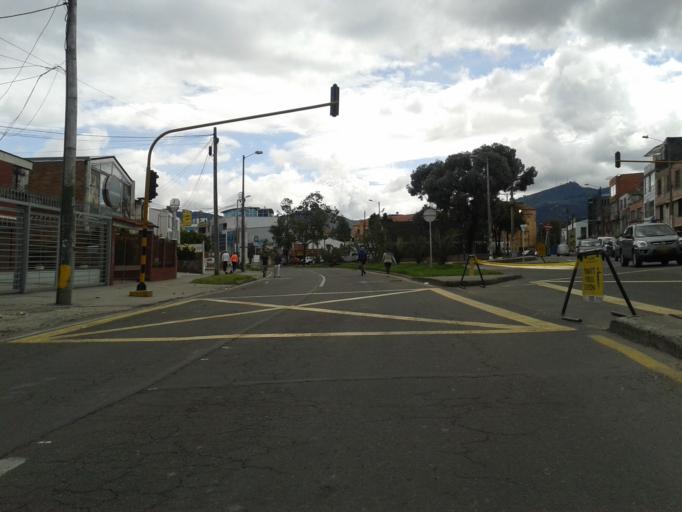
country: CO
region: Bogota D.C.
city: Barrio San Luis
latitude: 4.6989
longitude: -74.0766
